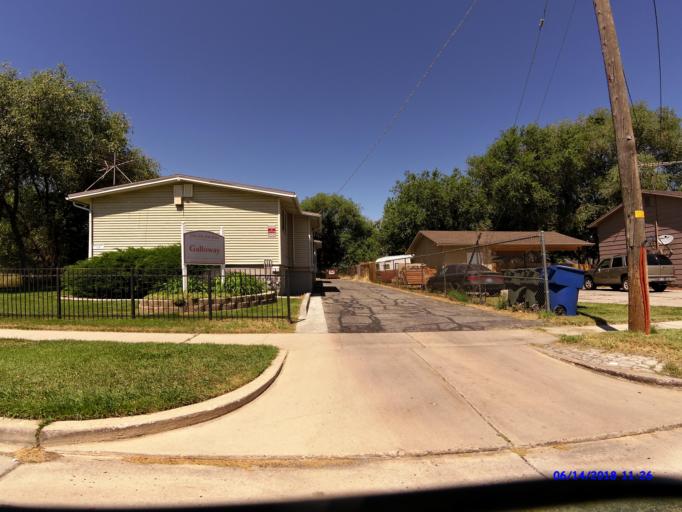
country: US
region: Utah
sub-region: Weber County
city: Ogden
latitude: 41.2205
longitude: -111.9942
